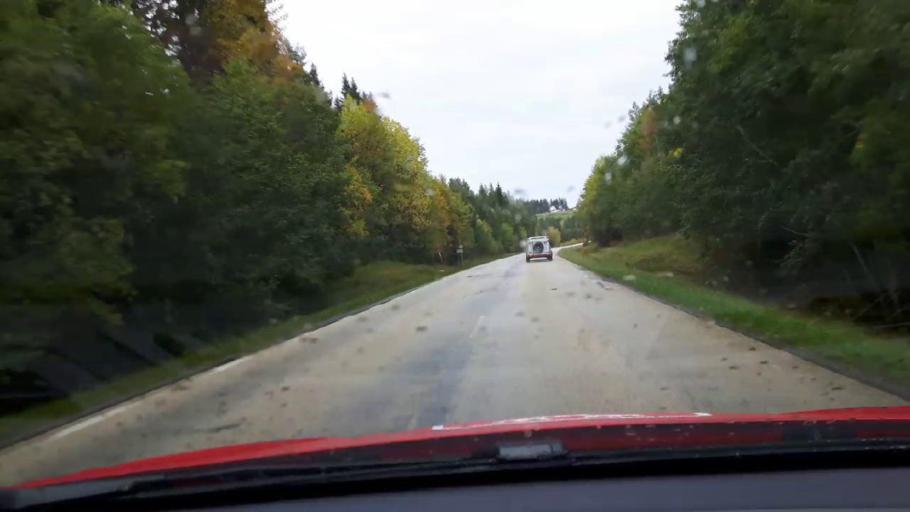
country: SE
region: Jaemtland
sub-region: Bergs Kommun
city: Hoverberg
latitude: 62.9521
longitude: 14.3390
